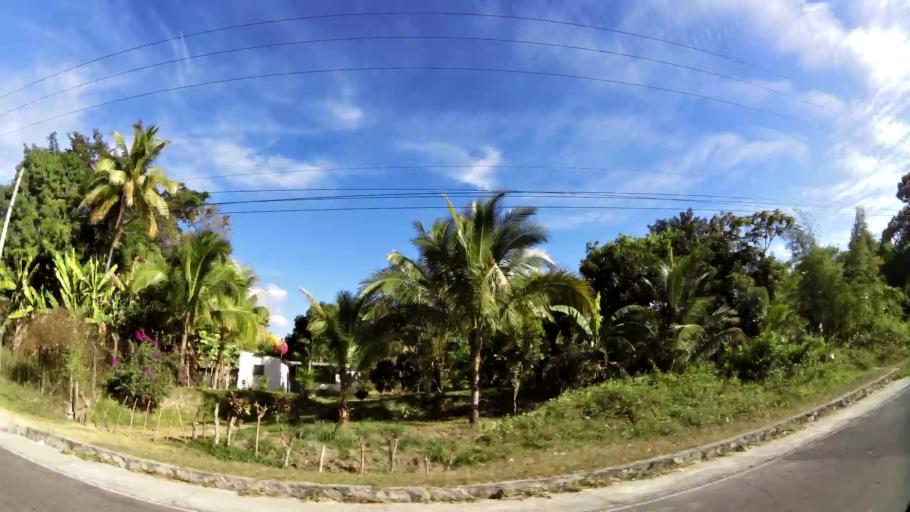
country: SV
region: Cuscatlan
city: Tecoluca
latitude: 13.7972
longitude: -89.0401
